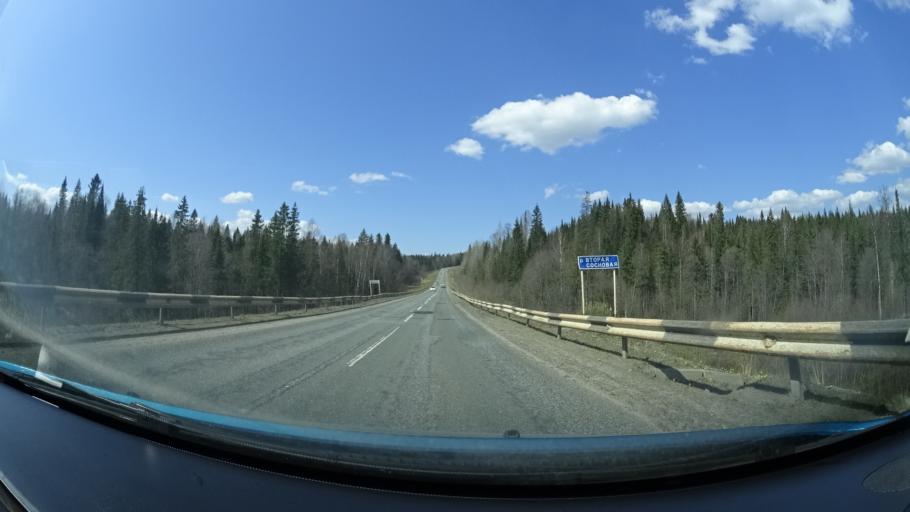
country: RU
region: Perm
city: Yugo-Kamskiy
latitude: 57.6138
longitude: 55.6324
